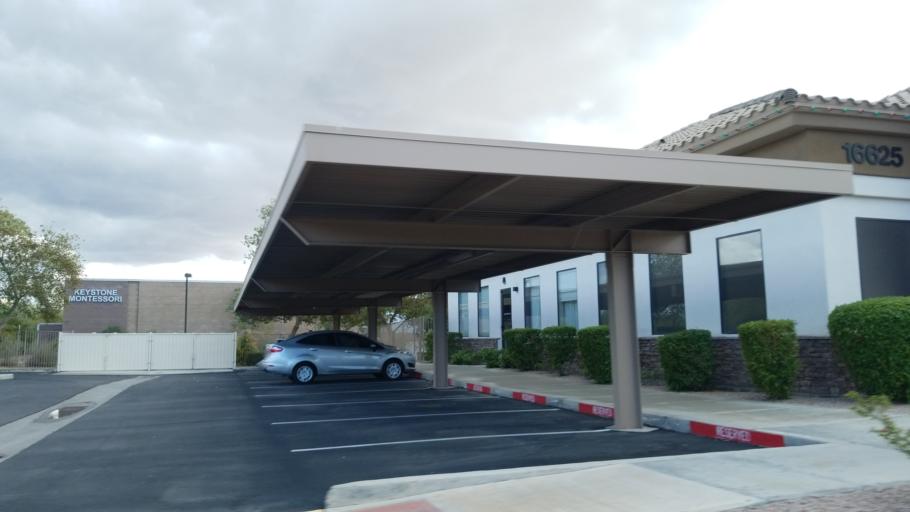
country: US
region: Arizona
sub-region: Maricopa County
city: Guadalupe
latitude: 33.2961
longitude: -112.0615
